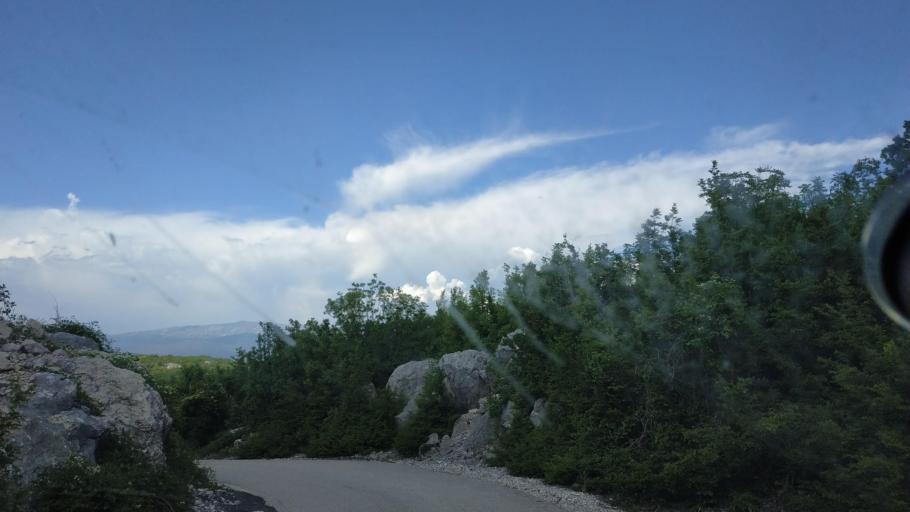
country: HR
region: Splitsko-Dalmatinska
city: Dugopolje
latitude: 43.5717
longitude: 16.6555
